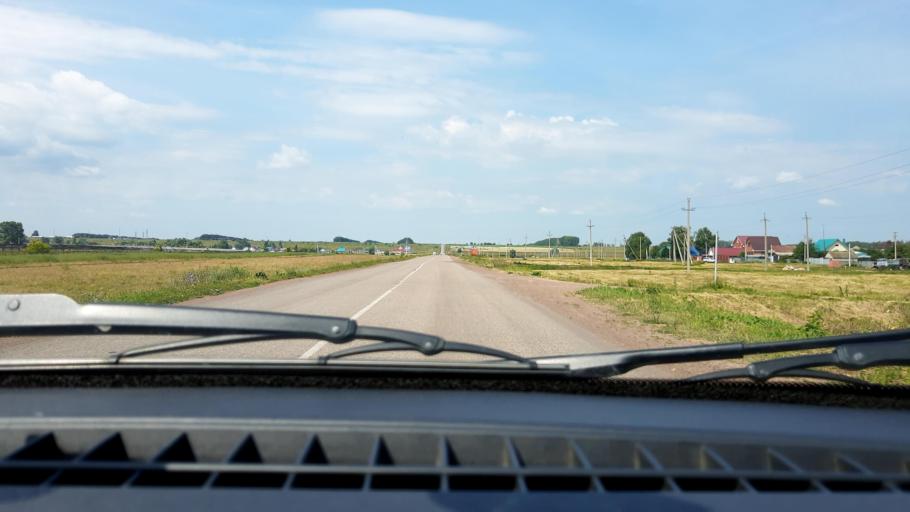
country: RU
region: Bashkortostan
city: Mikhaylovka
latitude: 54.8884
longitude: 55.8965
